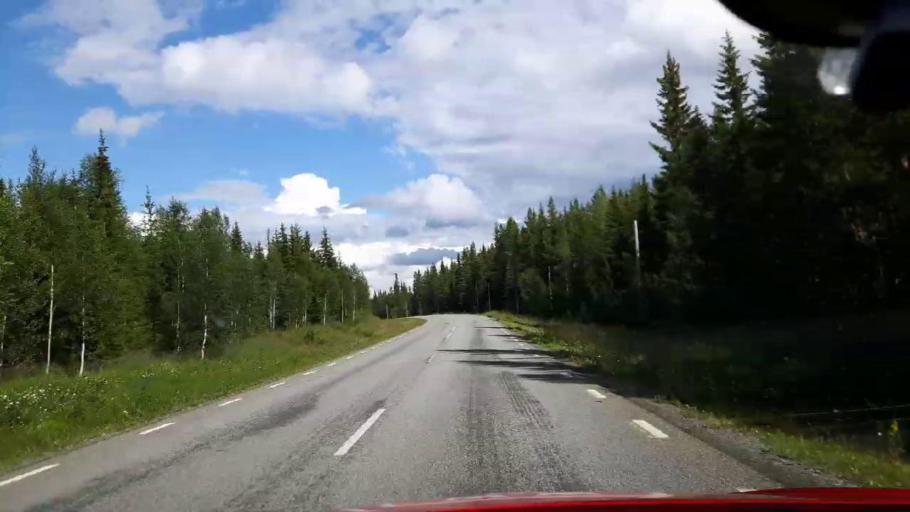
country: SE
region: Jaemtland
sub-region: Are Kommun
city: Are
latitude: 63.2236
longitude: 13.1240
